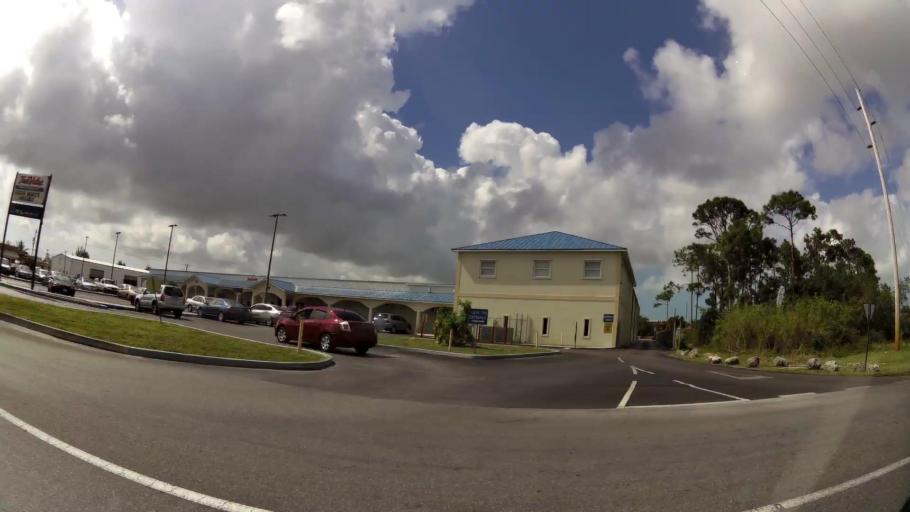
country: BS
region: Freeport
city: Freeport
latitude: 26.5378
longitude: -78.6986
